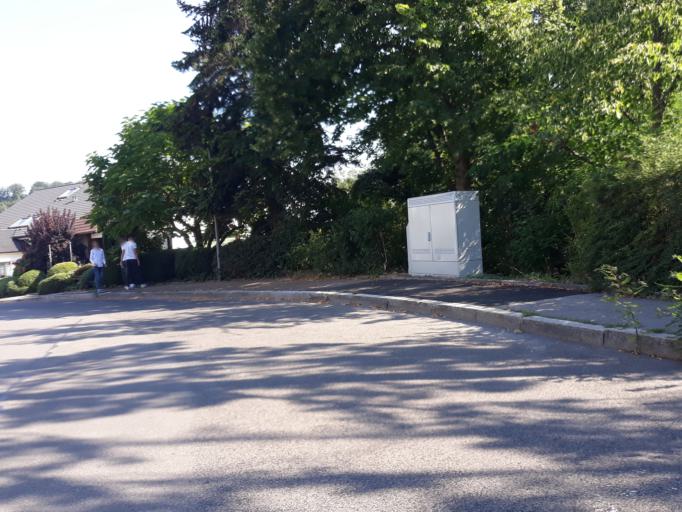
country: DE
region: Baden-Wuerttemberg
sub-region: Regierungsbezirk Stuttgart
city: Boeblingen
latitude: 48.6834
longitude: 9.0340
